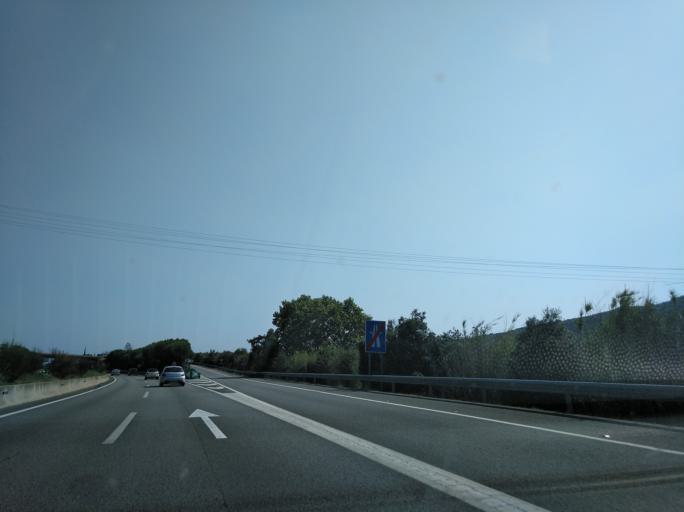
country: ES
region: Catalonia
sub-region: Provincia de Barcelona
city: Argentona
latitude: 41.5541
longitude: 2.4090
